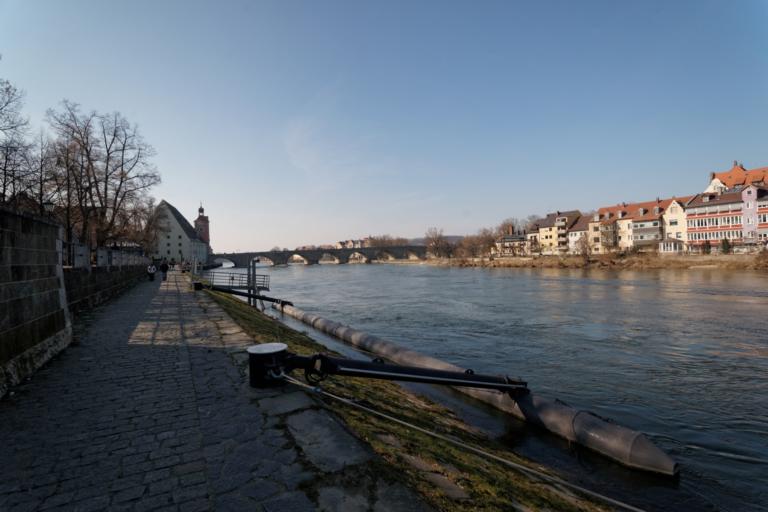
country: DE
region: Bavaria
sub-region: Upper Palatinate
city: Regensburg
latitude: 49.0208
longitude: 12.0998
